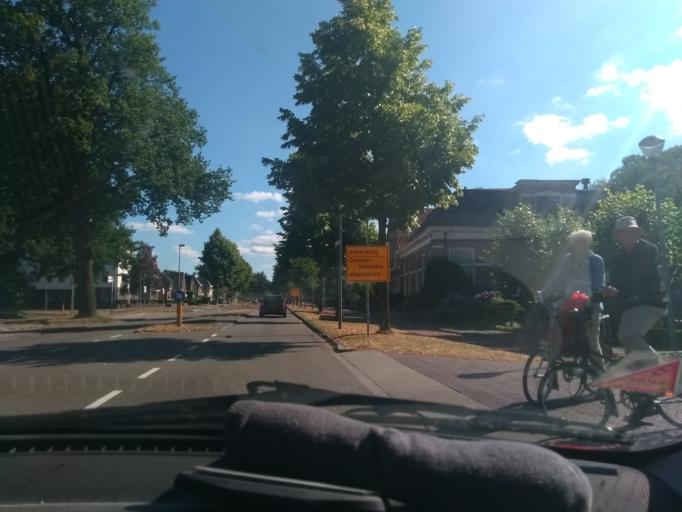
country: NL
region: Drenthe
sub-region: Gemeente Tynaarlo
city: Vries
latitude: 53.0785
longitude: 6.5796
